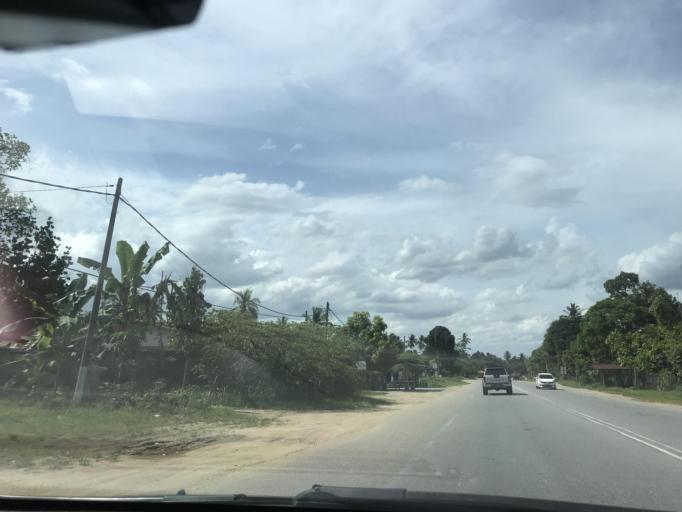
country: MY
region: Kelantan
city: Tanah Merah
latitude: 5.8452
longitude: 102.1618
